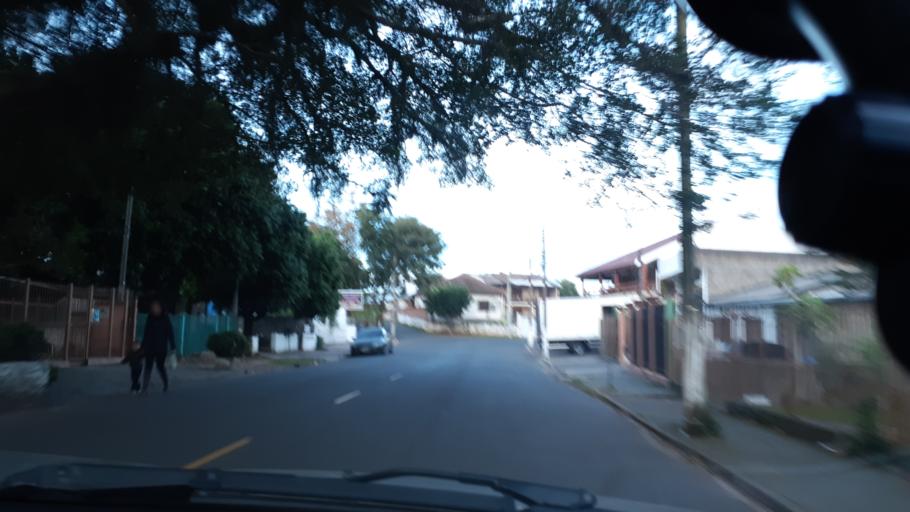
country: BR
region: Rio Grande do Sul
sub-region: Sapucaia Do Sul
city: Sapucaia
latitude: -29.8431
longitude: -51.1506
